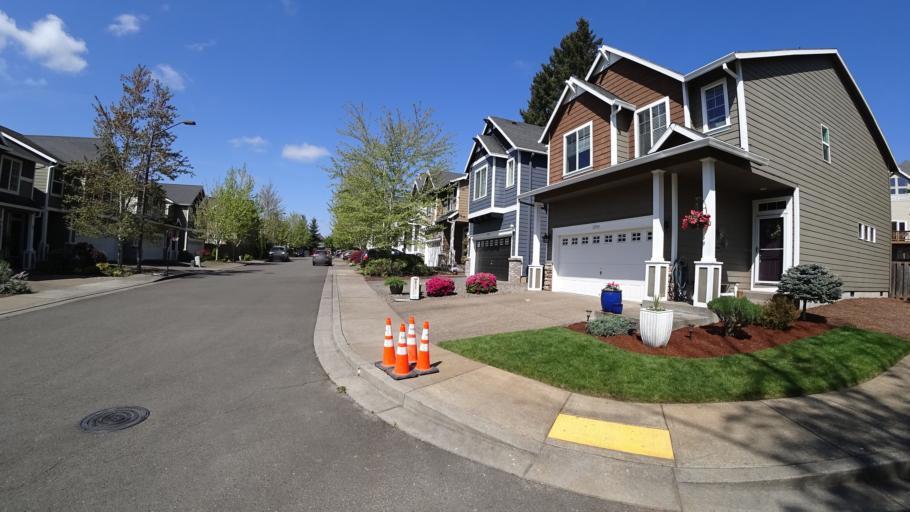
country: US
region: Oregon
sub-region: Washington County
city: King City
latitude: 45.4287
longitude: -122.8385
